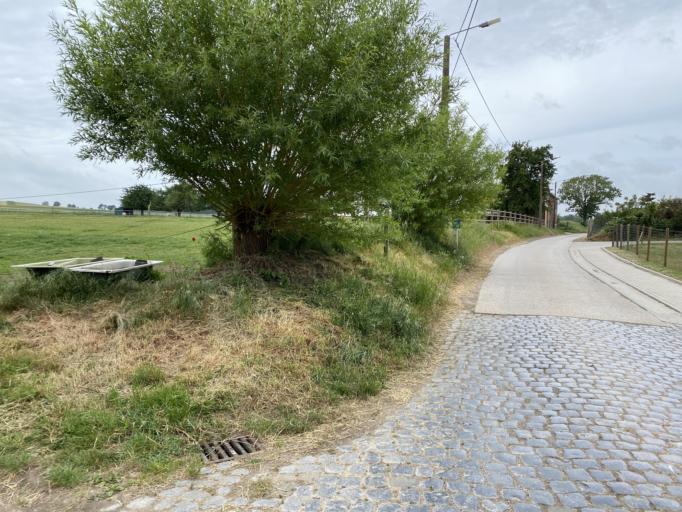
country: BE
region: Wallonia
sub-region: Province de Liege
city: Crisnee
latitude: 50.7567
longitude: 5.3752
